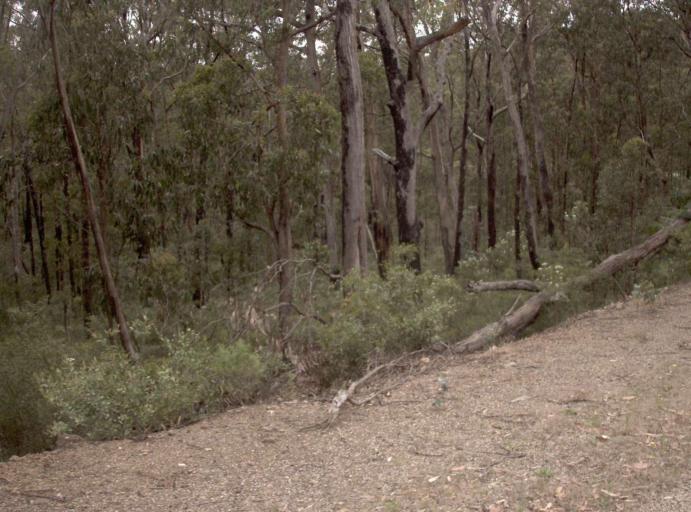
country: AU
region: Victoria
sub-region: East Gippsland
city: Bairnsdale
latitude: -37.5995
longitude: 147.1927
